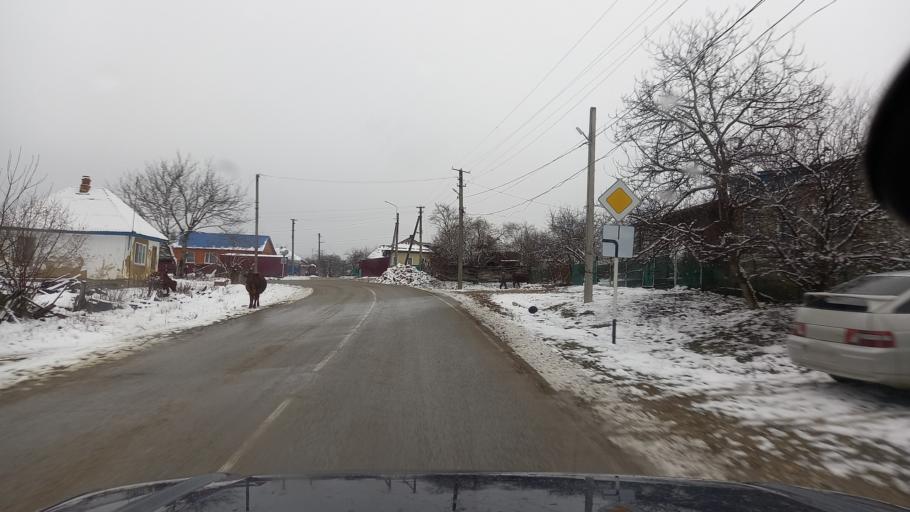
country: RU
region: Adygeya
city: Abadzekhskaya
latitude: 44.3557
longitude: 40.4083
